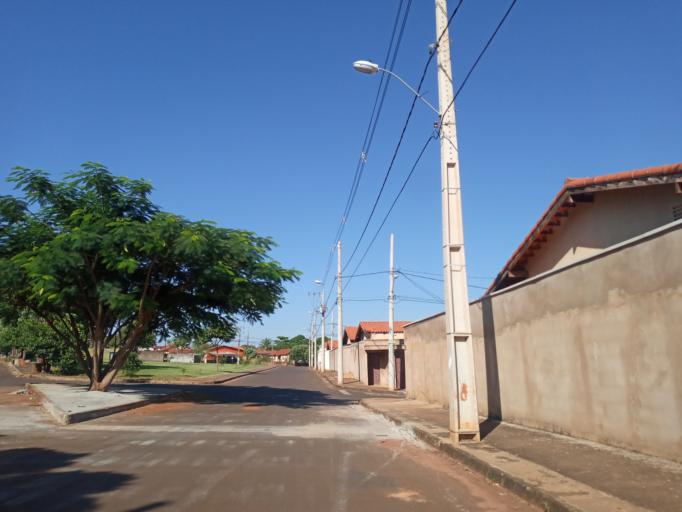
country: BR
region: Minas Gerais
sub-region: Ituiutaba
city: Ituiutaba
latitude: -18.9794
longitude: -49.4911
